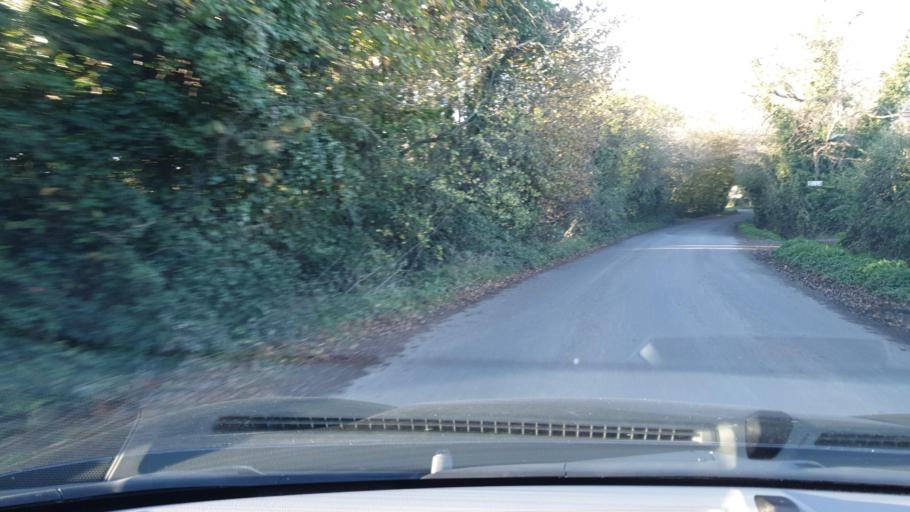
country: IE
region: Leinster
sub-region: An Mhi
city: Stamullin
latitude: 53.6217
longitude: -6.2623
